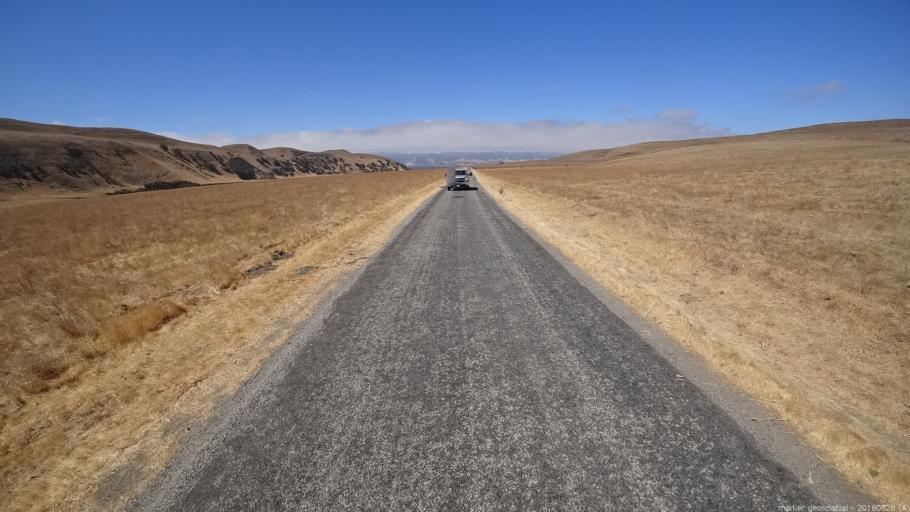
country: US
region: California
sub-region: San Luis Obispo County
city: Lake Nacimiento
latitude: 36.0339
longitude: -120.8496
